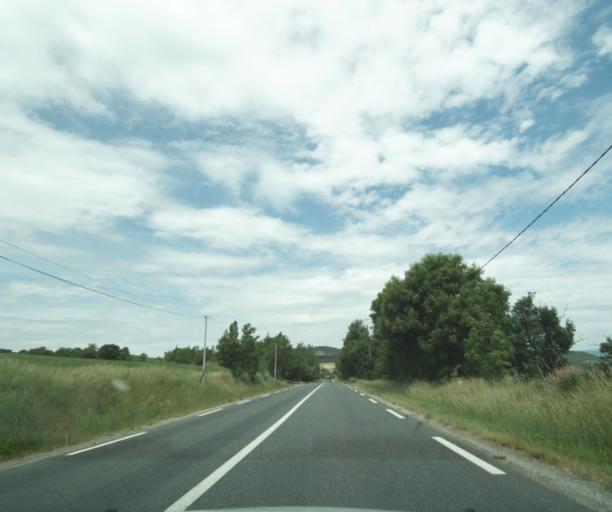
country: FR
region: Midi-Pyrenees
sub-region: Departement de l'Aveyron
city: Saint-Affrique
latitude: 43.9657
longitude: 2.9644
